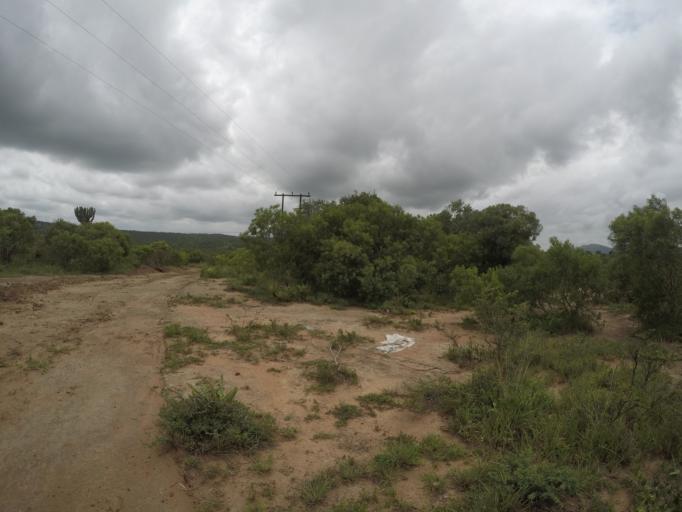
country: ZA
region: KwaZulu-Natal
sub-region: uThungulu District Municipality
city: Empangeni
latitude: -28.6020
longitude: 31.8298
